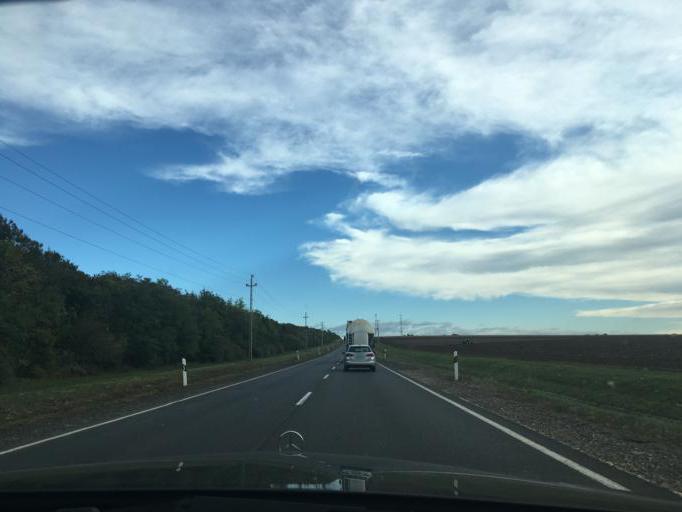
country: HU
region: Borsod-Abauj-Zemplen
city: Arnot
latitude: 48.1445
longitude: 20.8890
